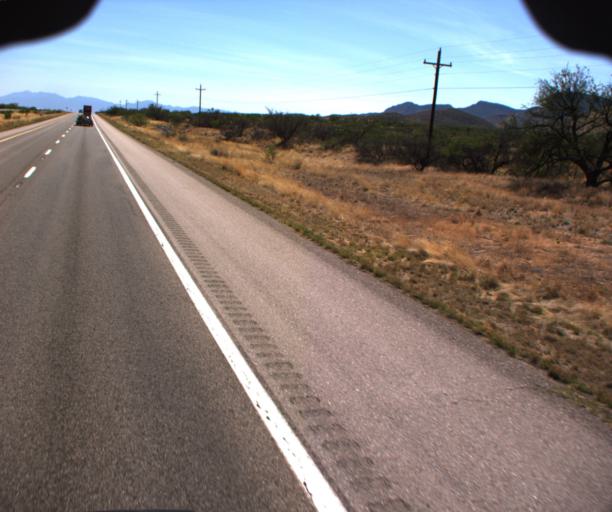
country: US
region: Arizona
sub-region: Cochise County
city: Whetstone
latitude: 31.8643
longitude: -110.3413
